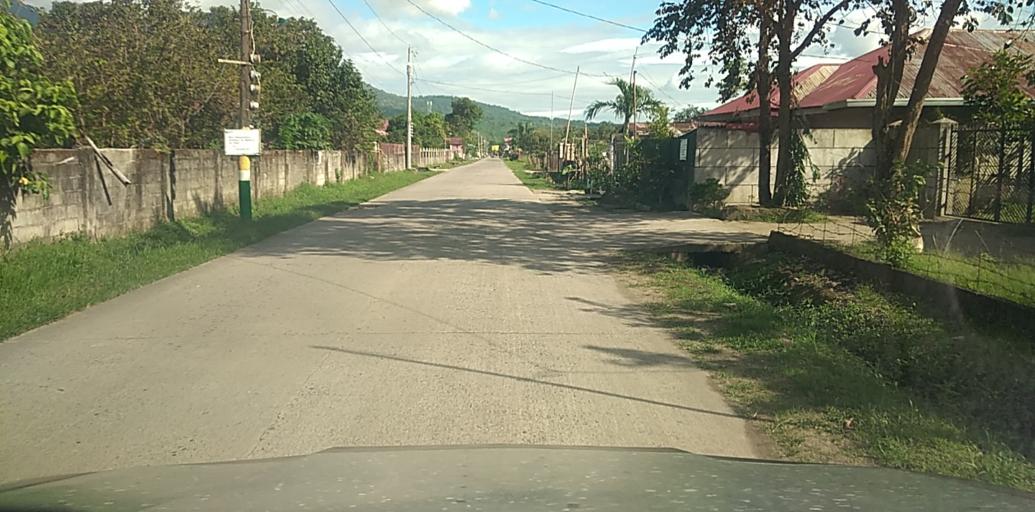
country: PH
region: Central Luzon
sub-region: Province of Pampanga
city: Buensuseso
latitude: 15.1926
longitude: 120.6838
